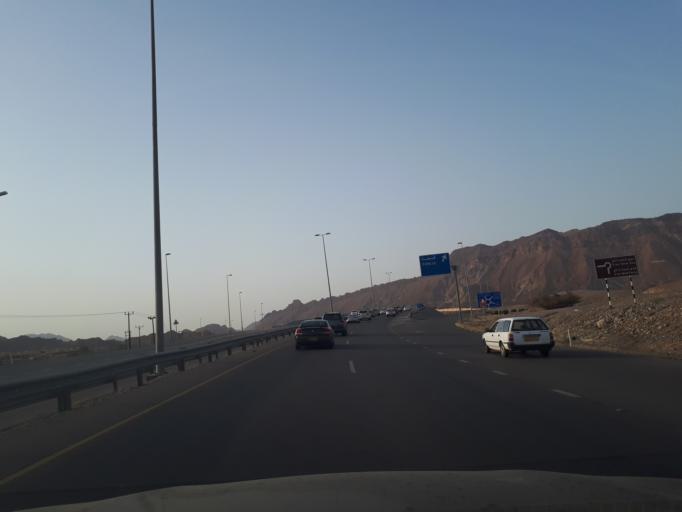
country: OM
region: Muhafazat ad Dakhiliyah
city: Bidbid
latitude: 23.4302
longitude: 58.1202
